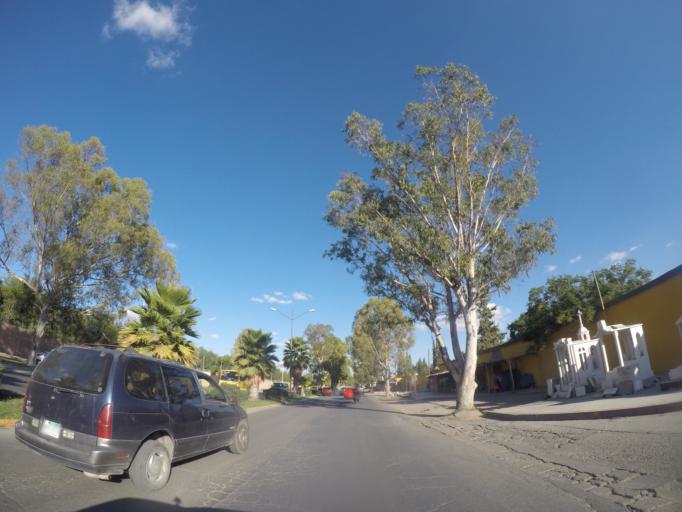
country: MX
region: San Luis Potosi
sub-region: San Luis Potosi
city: San Luis Potosi
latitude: 22.1805
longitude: -100.9969
